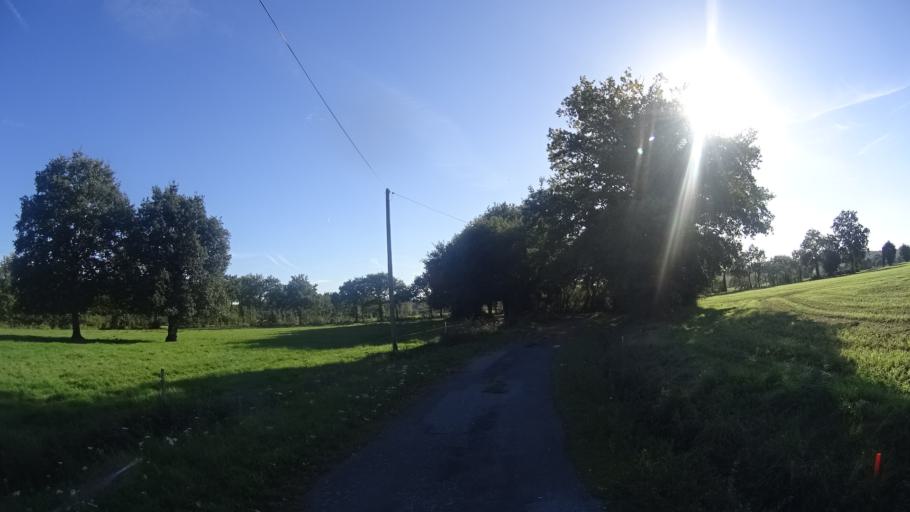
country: FR
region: Brittany
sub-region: Departement du Morbihan
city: Saint-Jacut-les-Pins
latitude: 47.6982
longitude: -2.1860
